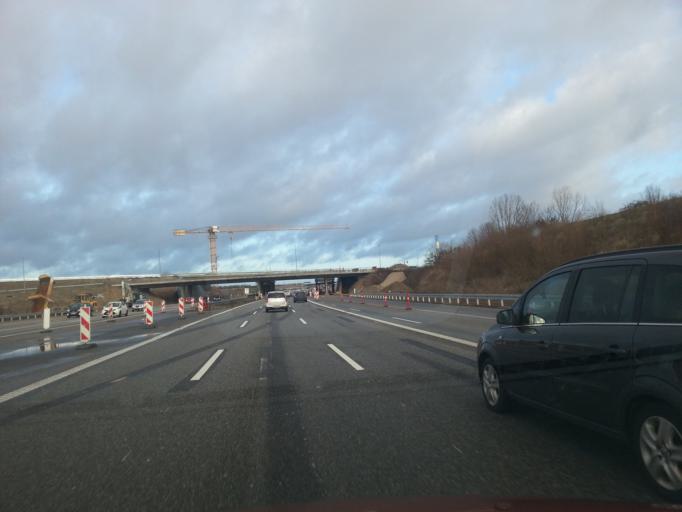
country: DK
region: Zealand
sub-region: Solrod Kommune
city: Solrod
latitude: 55.5344
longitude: 12.1989
